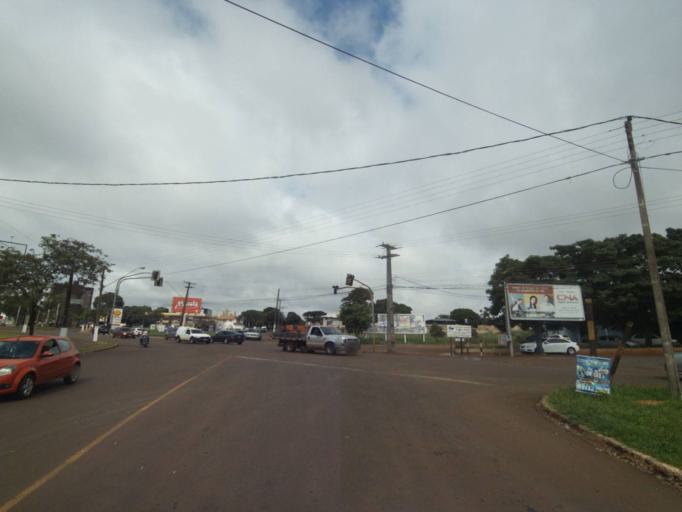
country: BR
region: Parana
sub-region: Campo Mourao
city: Campo Mourao
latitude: -24.0322
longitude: -52.3660
